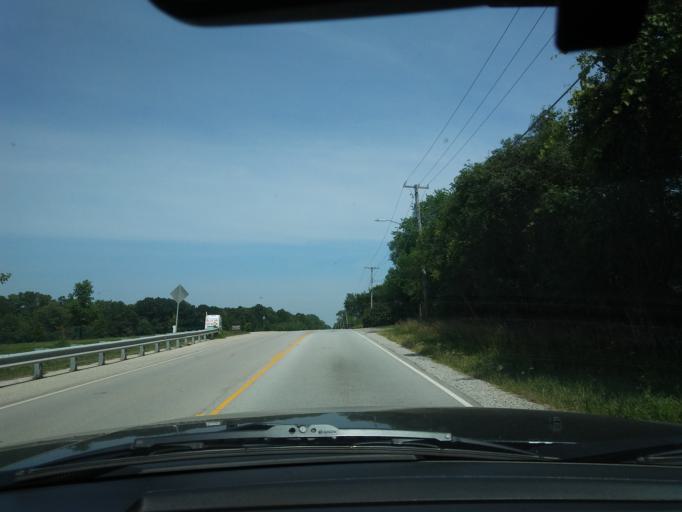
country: US
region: Illinois
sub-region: Cook County
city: Oak Forest
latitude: 41.6246
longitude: -87.7700
